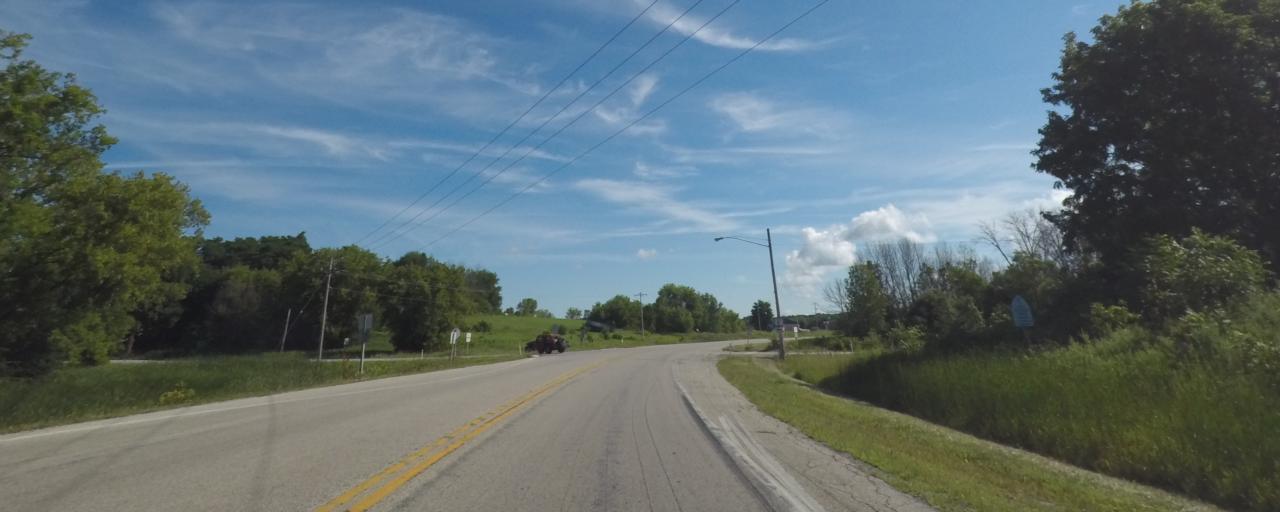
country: US
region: Wisconsin
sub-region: Jefferson County
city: Ixonia
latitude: 43.0700
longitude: -88.6003
